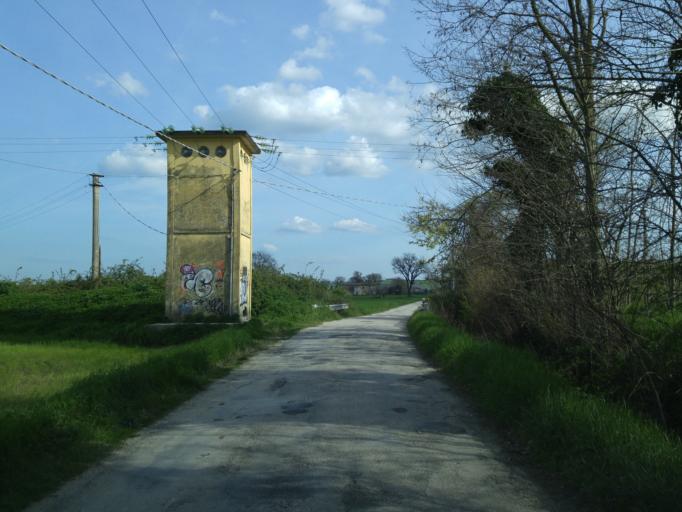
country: IT
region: The Marches
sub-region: Provincia di Pesaro e Urbino
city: Rosciano
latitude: 43.8080
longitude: 12.9945
